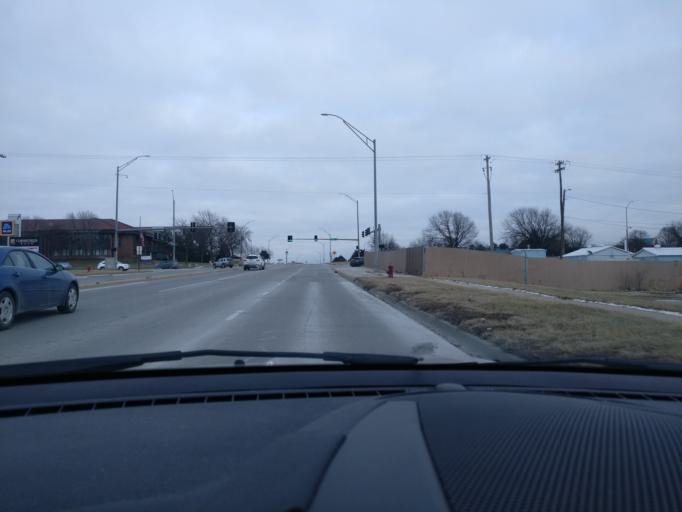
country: US
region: Nebraska
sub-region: Lancaster County
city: Lincoln
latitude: 40.8134
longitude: -96.6072
